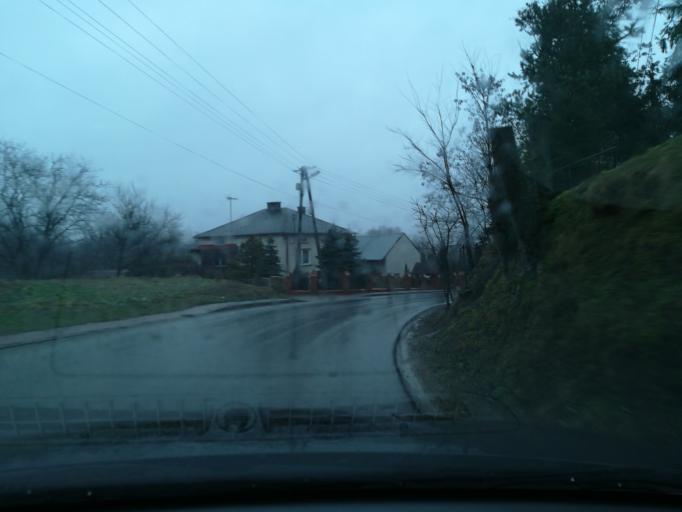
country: PL
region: Subcarpathian Voivodeship
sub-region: Powiat lancucki
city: Kosina
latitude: 50.0752
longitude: 22.3279
